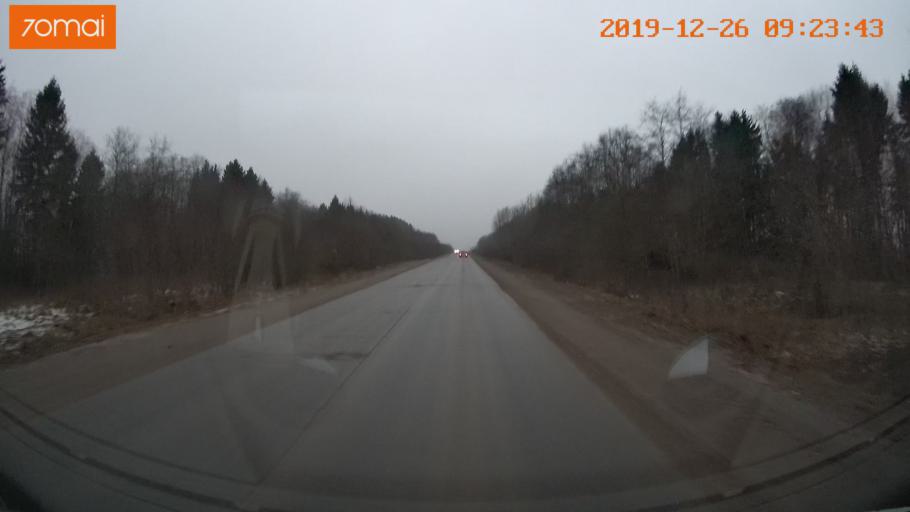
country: RU
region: Vologda
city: Gryazovets
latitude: 58.9923
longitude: 40.2070
